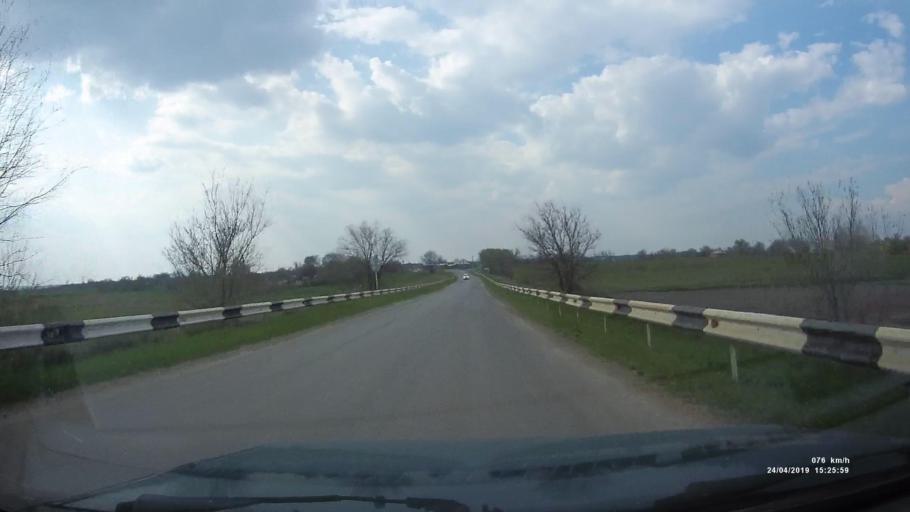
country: RU
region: Rostov
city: Remontnoye
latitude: 46.5553
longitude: 43.0389
